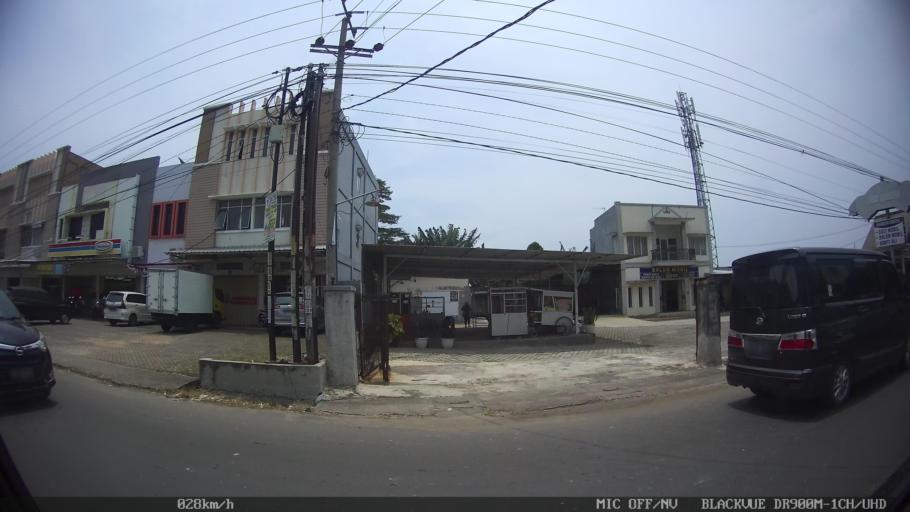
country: ID
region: Lampung
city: Bandarlampung
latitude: -5.4124
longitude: 105.2763
